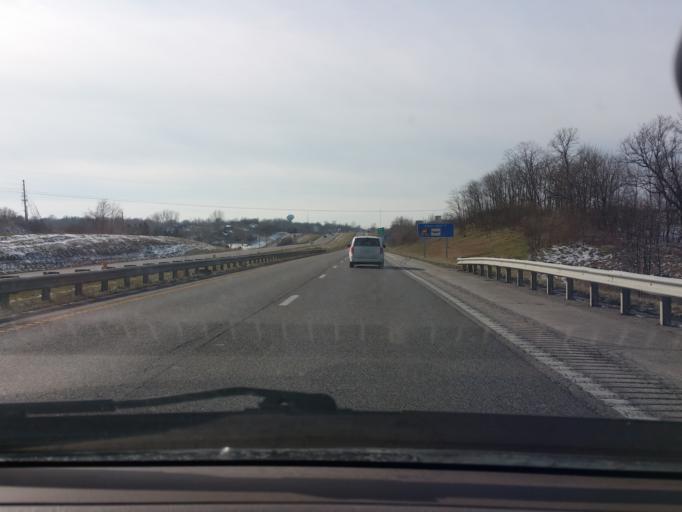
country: US
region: Missouri
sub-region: Clay County
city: Liberty
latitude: 39.2743
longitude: -94.4294
